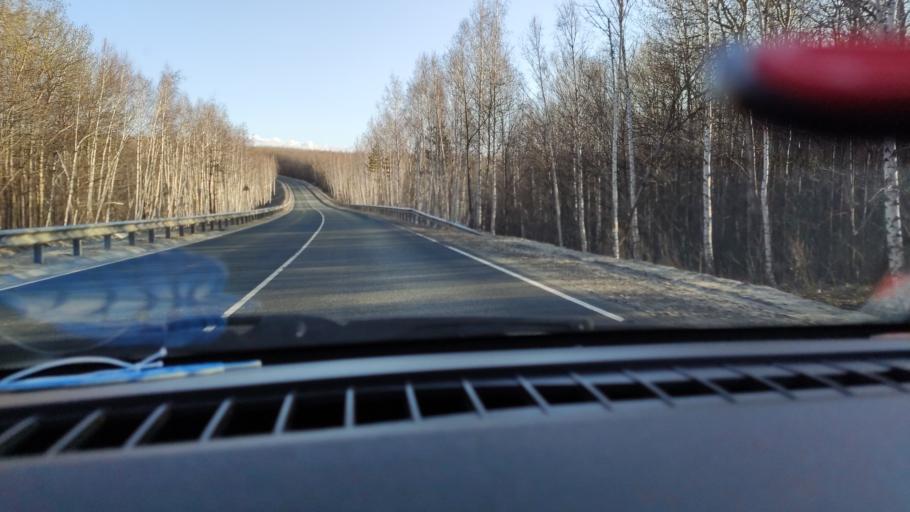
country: RU
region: Saratov
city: Khvalynsk
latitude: 52.4604
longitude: 48.0171
